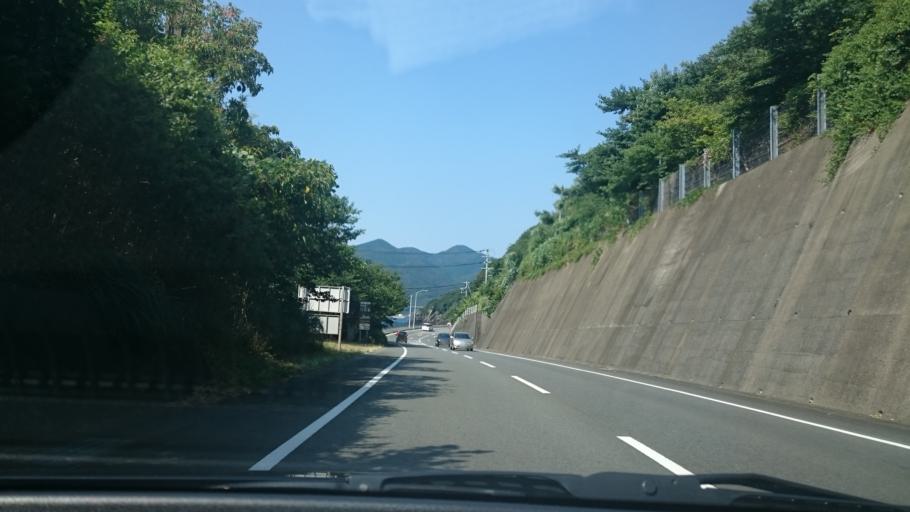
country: JP
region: Shizuoka
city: Heda
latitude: 34.8975
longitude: 138.7788
